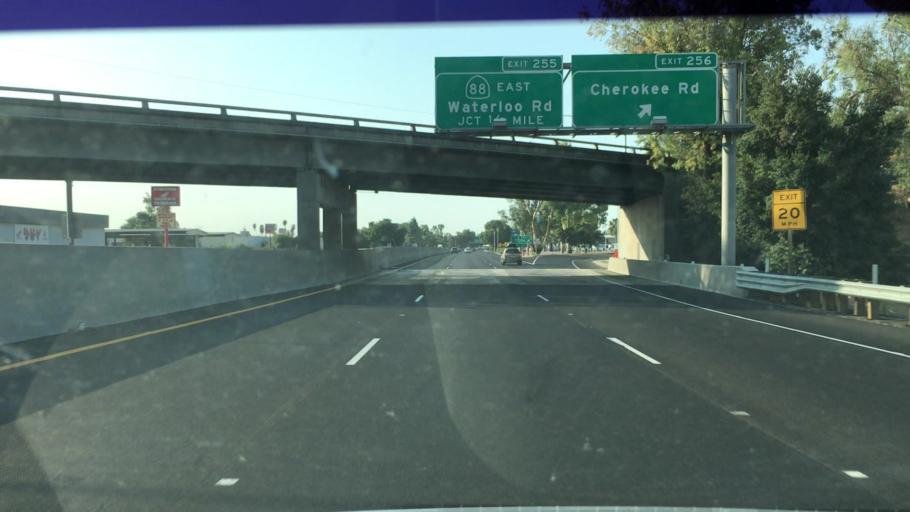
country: US
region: California
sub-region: San Joaquin County
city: August
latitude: 37.9924
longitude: -121.2529
